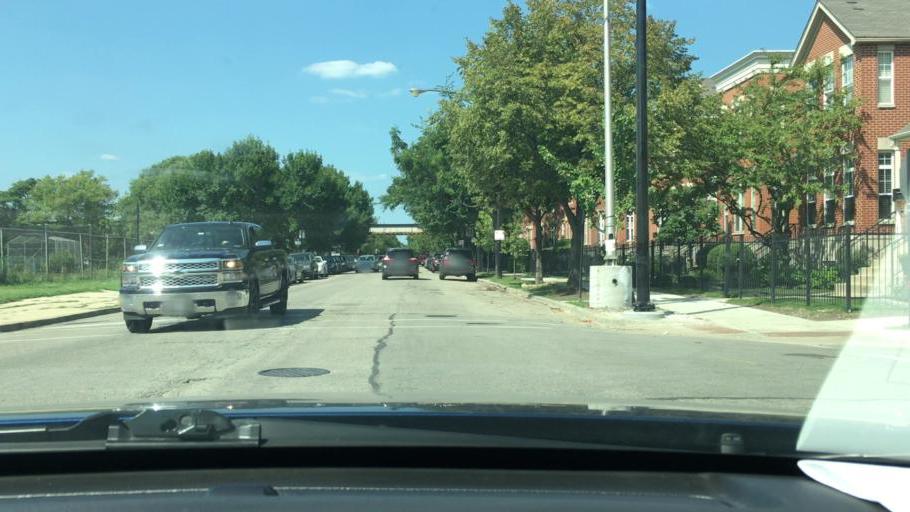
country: US
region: Illinois
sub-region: Cook County
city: Chicago
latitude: 41.9091
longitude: -87.6433
